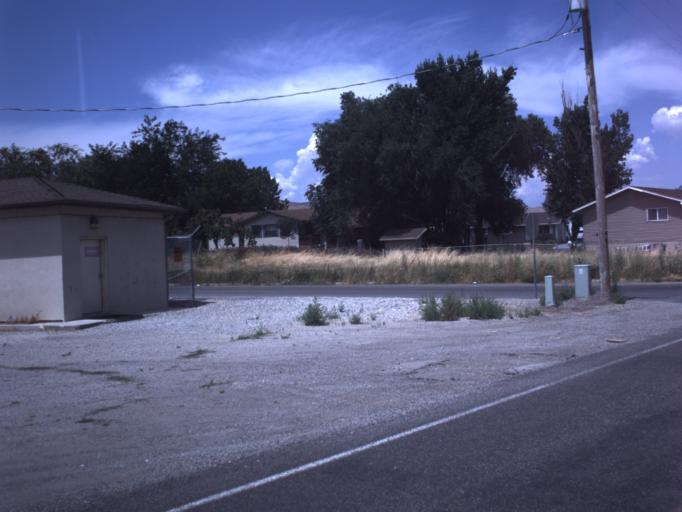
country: US
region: Utah
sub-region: Box Elder County
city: Tremonton
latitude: 41.6926
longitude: -112.2953
